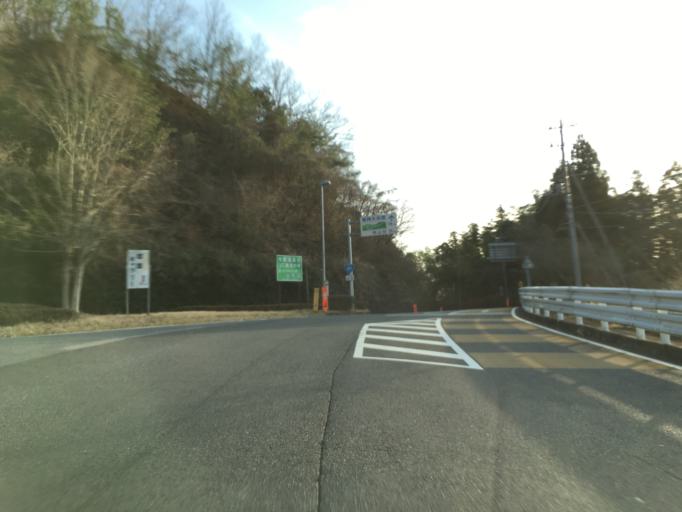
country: JP
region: Ibaraki
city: Daigo
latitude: 36.7581
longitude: 140.3907
